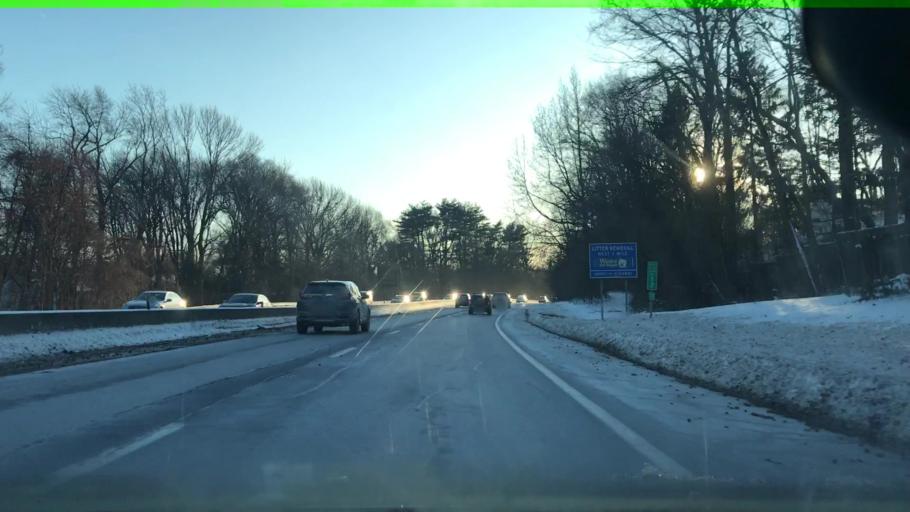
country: US
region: New York
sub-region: Westchester County
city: Scarsdale
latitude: 40.9644
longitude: -73.7843
